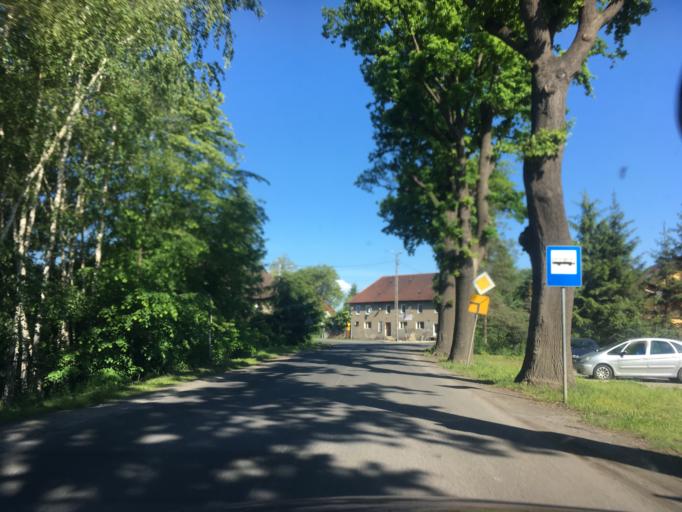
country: PL
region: Lower Silesian Voivodeship
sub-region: Powiat zgorzelecki
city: Sulikow
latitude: 51.0795
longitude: 15.0579
